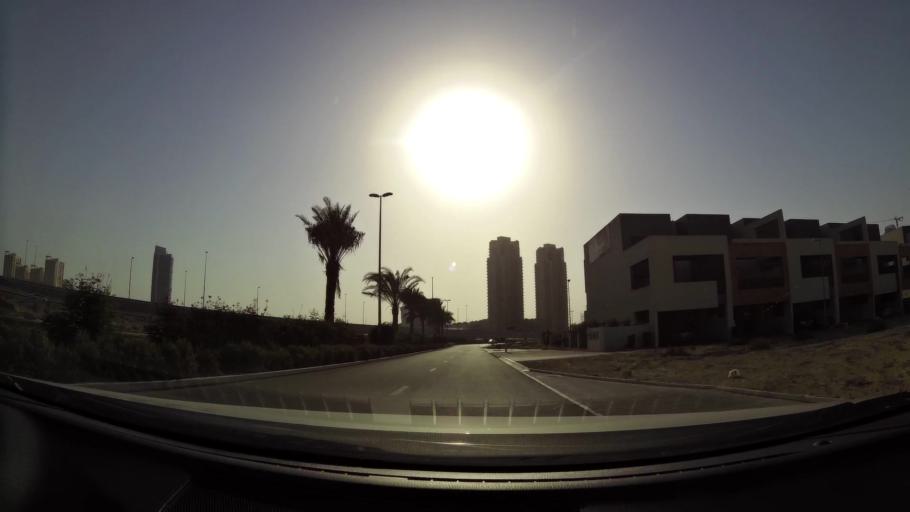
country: AE
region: Dubai
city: Dubai
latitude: 25.0464
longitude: 55.2005
